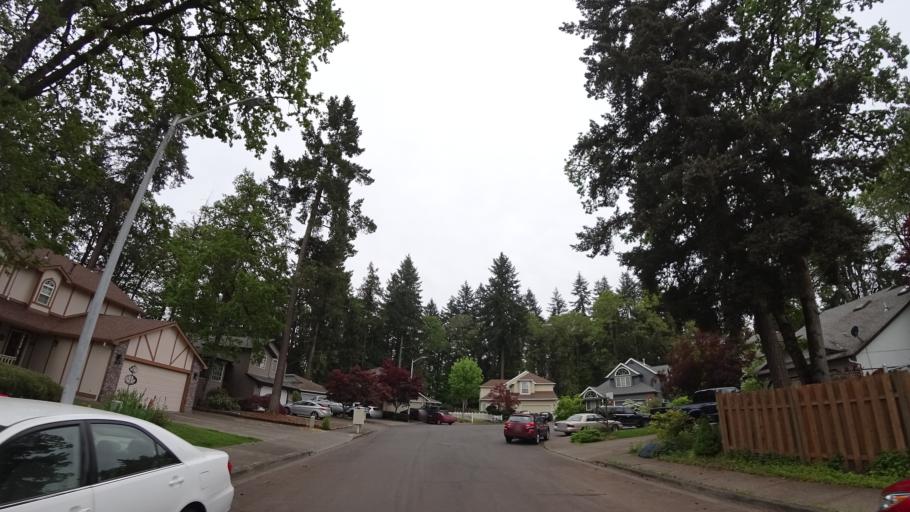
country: US
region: Oregon
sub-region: Washington County
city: Aloha
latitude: 45.5047
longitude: -122.9082
